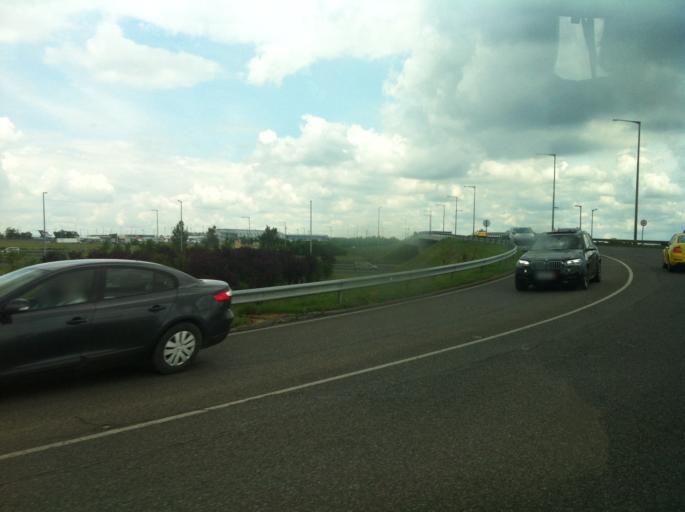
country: HU
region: Pest
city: Vecses
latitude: 47.4214
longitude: 19.2654
